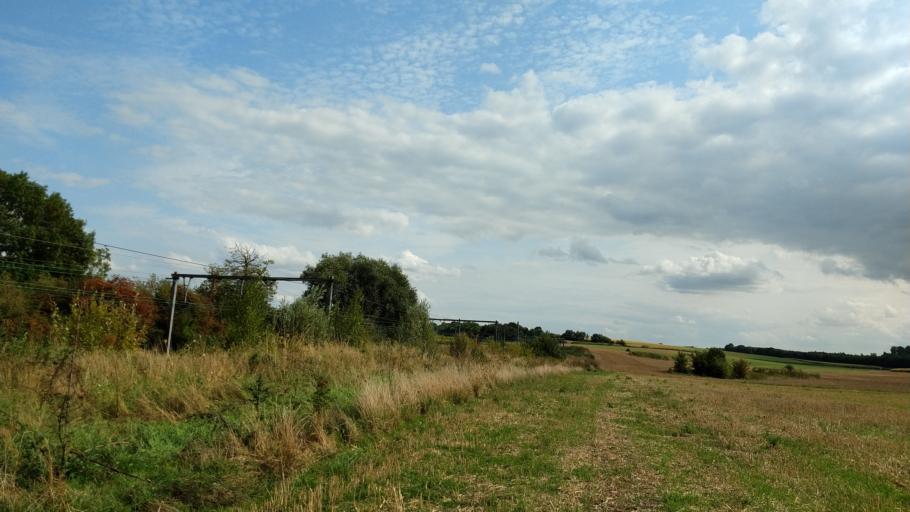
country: BE
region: Flanders
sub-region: Provincie Vlaams-Brabant
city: Boutersem
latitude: 50.8277
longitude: 4.8650
